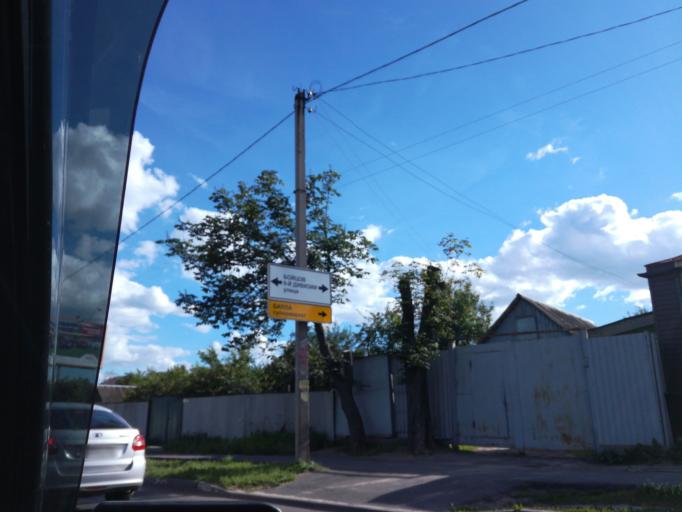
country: RU
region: Kursk
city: Kursk
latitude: 51.7325
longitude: 36.1551
